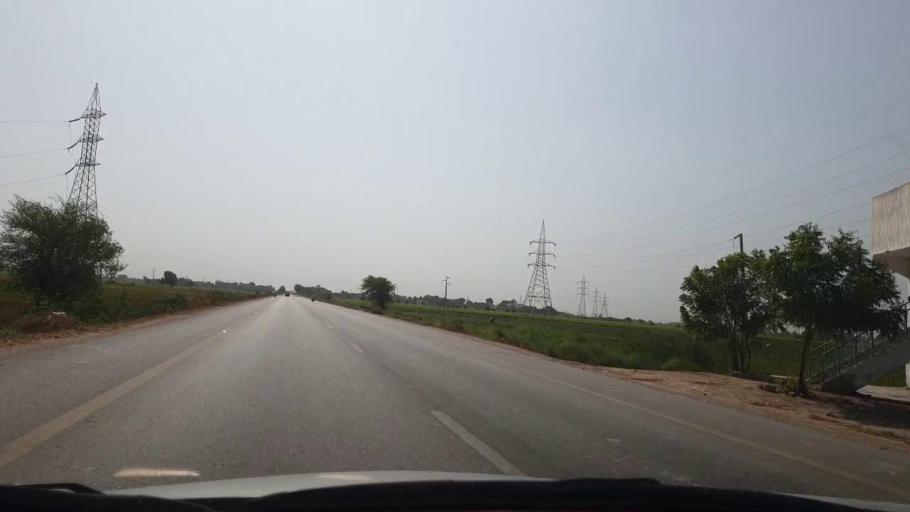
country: PK
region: Sindh
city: Tando Muhammad Khan
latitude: 25.1251
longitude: 68.5659
